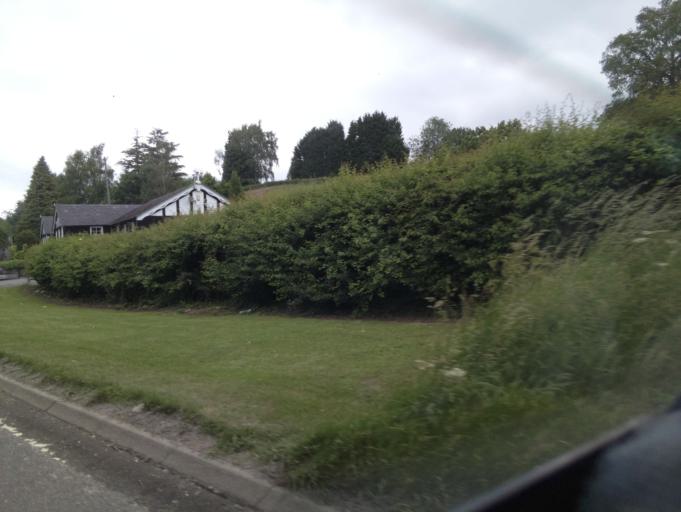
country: GB
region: England
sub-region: Staffordshire
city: Mayfield
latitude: 53.0002
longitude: -1.7514
